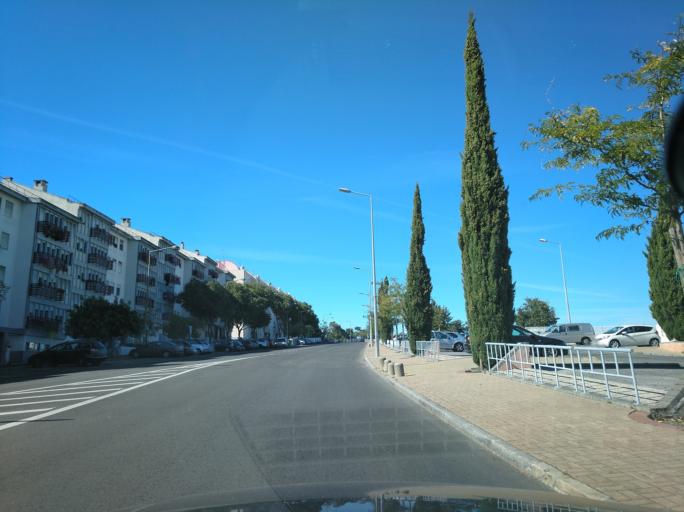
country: PT
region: Lisbon
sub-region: Loures
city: Moscavide
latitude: 38.7532
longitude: -9.1227
